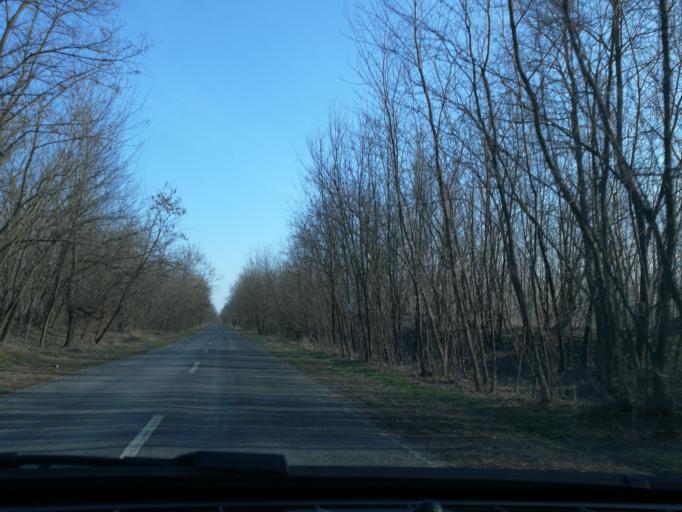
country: HU
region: Szabolcs-Szatmar-Bereg
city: Nyirbogdany
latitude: 48.0320
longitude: 21.9272
